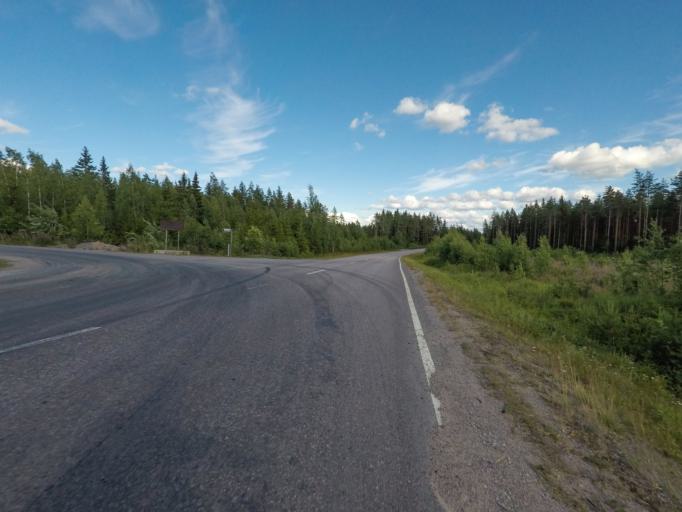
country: FI
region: South Karelia
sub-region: Lappeenranta
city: Joutseno
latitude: 61.1463
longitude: 28.6220
